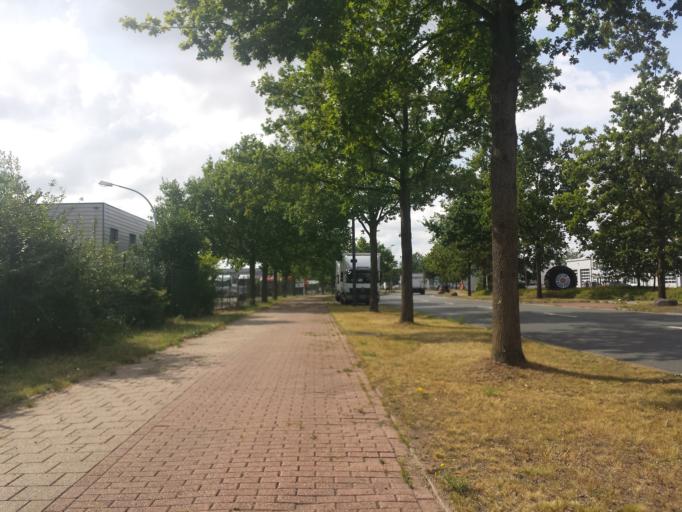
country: DE
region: Lower Saxony
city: Stuhr
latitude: 53.0866
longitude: 8.7145
